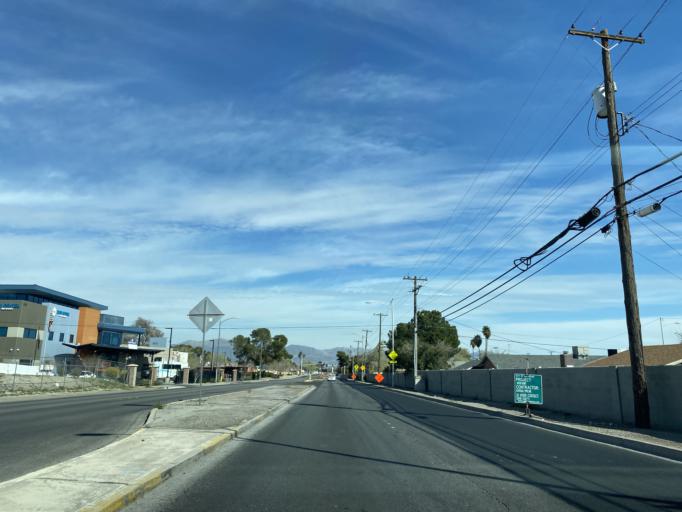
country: US
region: Nevada
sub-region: Clark County
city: Las Vegas
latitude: 36.1817
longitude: -115.1250
